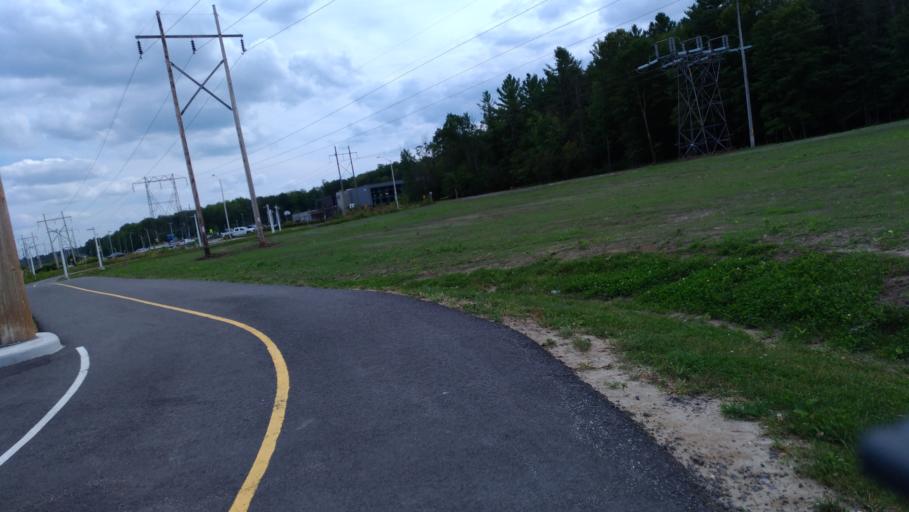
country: CA
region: Ontario
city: Bells Corners
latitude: 45.3430
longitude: -75.9325
